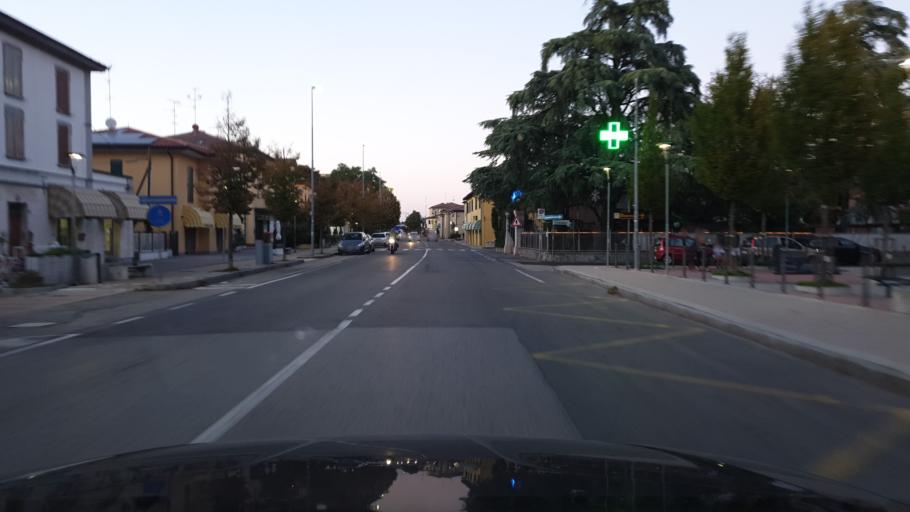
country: IT
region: Emilia-Romagna
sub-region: Provincia di Bologna
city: Altedo
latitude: 44.6658
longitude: 11.4875
